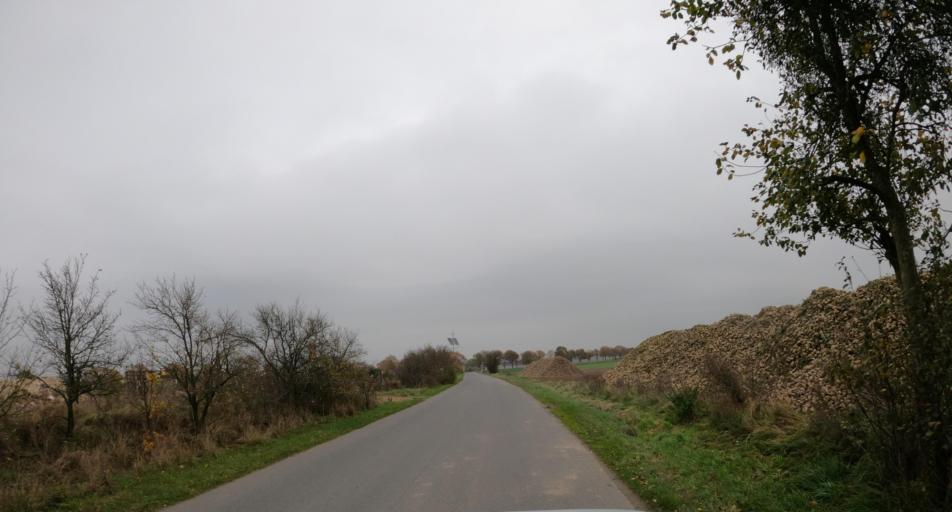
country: PL
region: West Pomeranian Voivodeship
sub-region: Powiat stargardzki
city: Suchan
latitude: 53.2727
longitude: 15.4098
